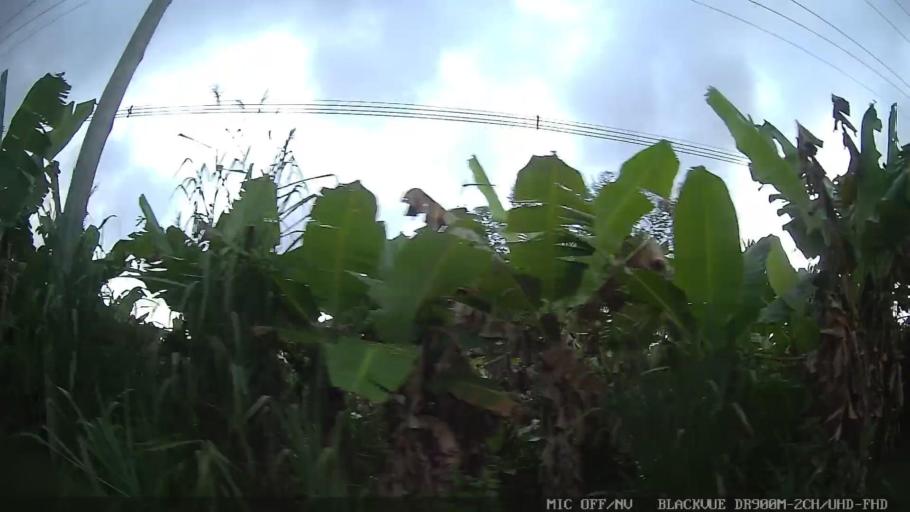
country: BR
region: Sao Paulo
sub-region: Itanhaem
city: Itanhaem
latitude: -24.0896
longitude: -46.7971
